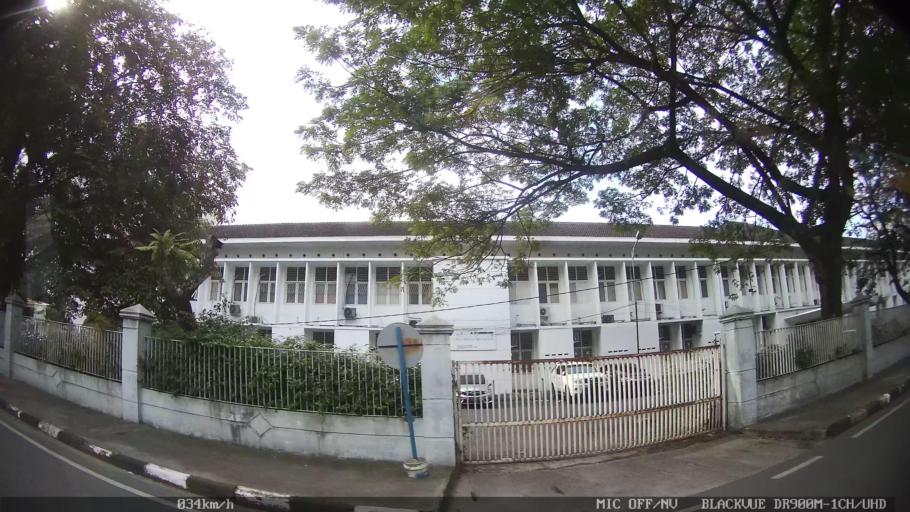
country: ID
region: North Sumatra
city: Medan
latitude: 3.5979
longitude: 98.6897
